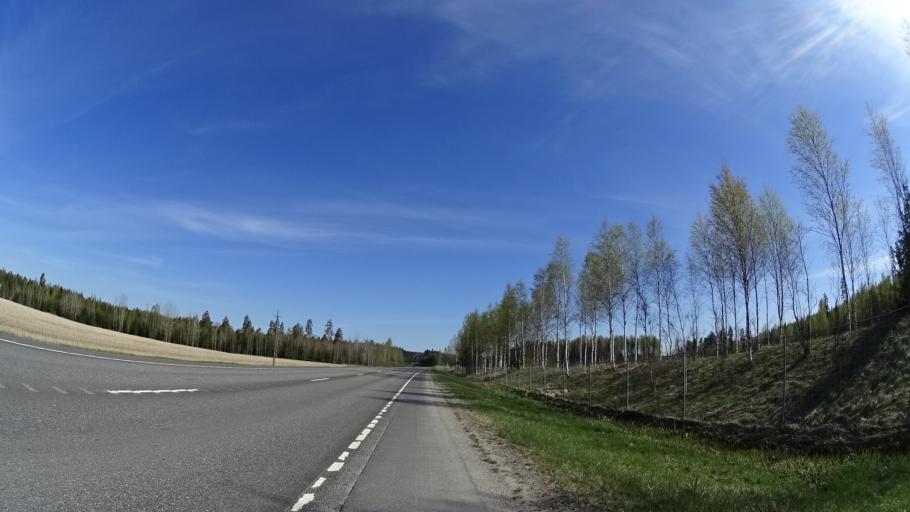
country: FI
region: Uusimaa
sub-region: Helsinki
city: Nurmijaervi
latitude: 60.4233
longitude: 24.8245
